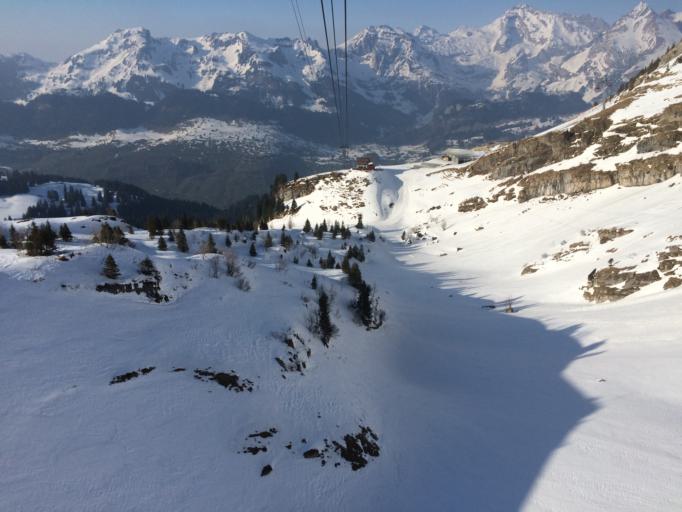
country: CH
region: Saint Gallen
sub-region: Wahlkreis Sarganserland
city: Walenstadt
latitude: 47.1668
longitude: 9.3120
